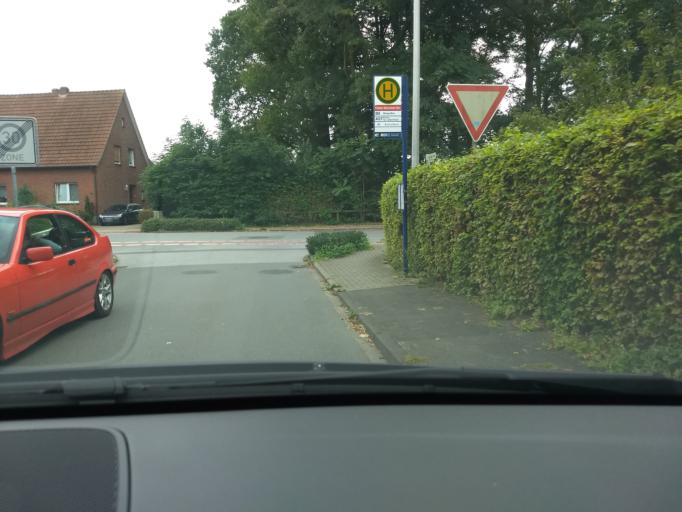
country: DE
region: North Rhine-Westphalia
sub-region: Regierungsbezirk Munster
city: Borken
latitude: 51.8458
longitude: 6.8767
